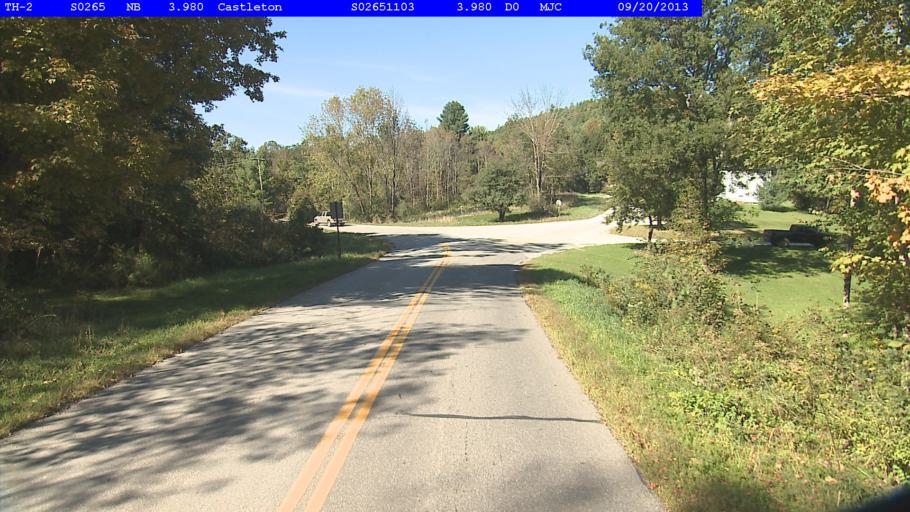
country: US
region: Vermont
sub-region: Rutland County
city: Castleton
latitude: 43.6572
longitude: -73.2298
